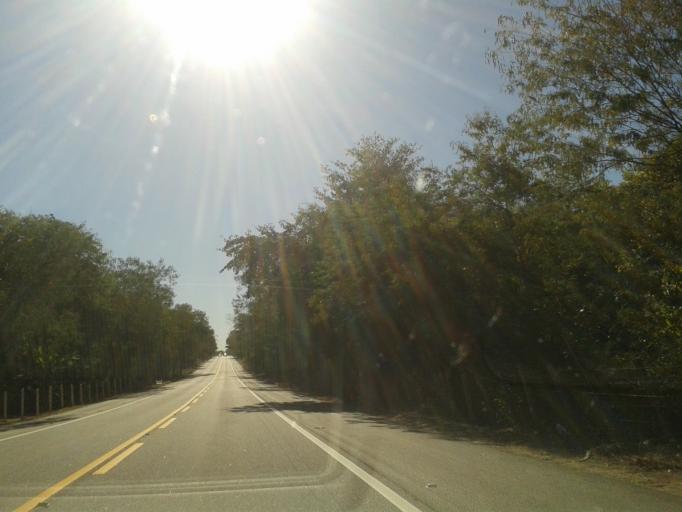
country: BR
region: Goias
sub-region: Itapuranga
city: Itapuranga
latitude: -15.4800
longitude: -50.3337
